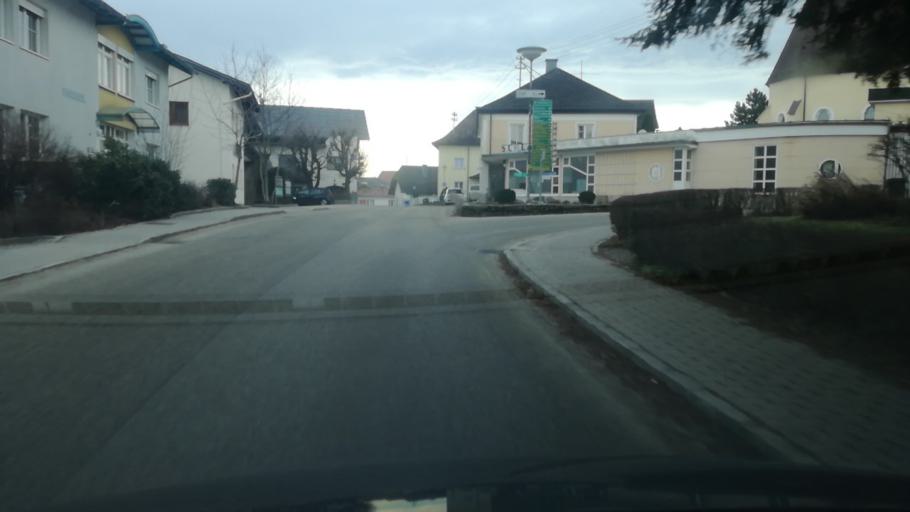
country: AT
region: Upper Austria
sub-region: Politischer Bezirk Vocklabruck
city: Neukirchen an der Vockla
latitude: 48.0412
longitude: 13.5383
